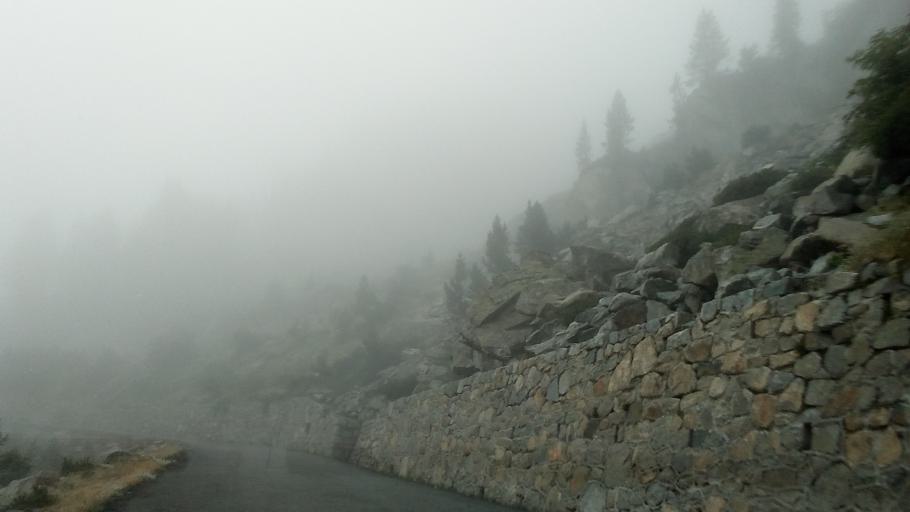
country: FR
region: Midi-Pyrenees
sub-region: Departement des Hautes-Pyrenees
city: Luz-Saint-Sauveur
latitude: 42.8190
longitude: 0.1425
